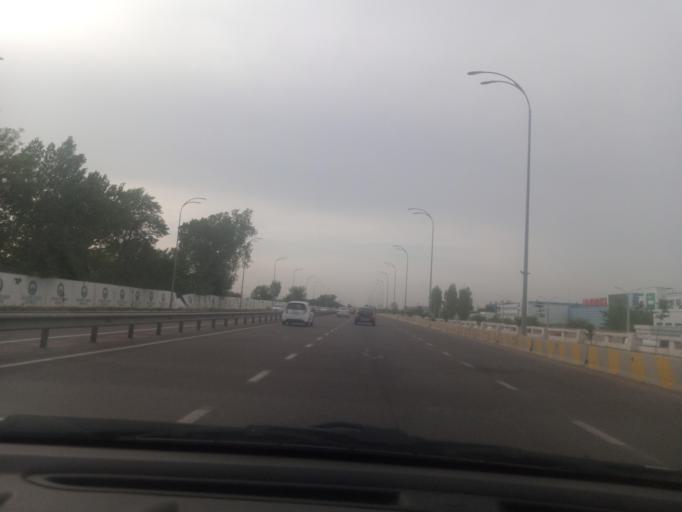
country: UZ
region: Toshkent Shahri
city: Bektemir
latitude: 41.2658
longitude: 69.3692
